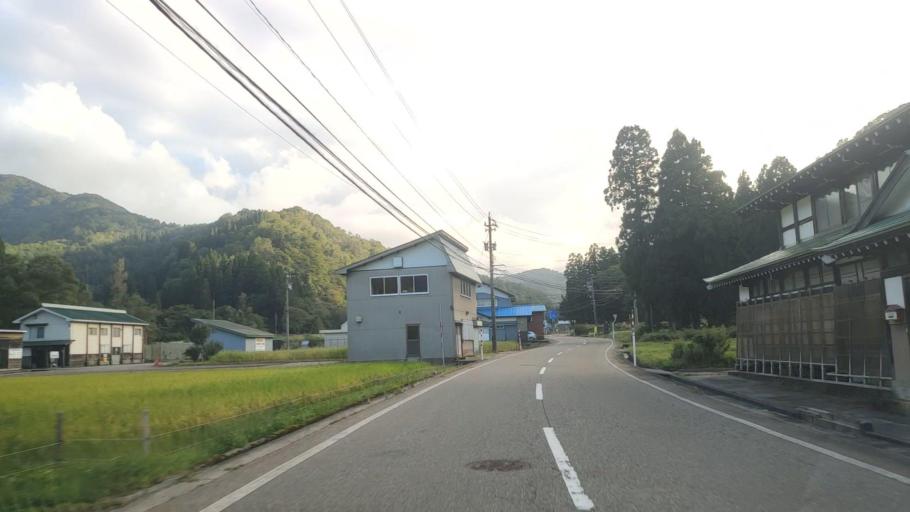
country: JP
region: Toyama
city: Yatsuomachi-higashikumisaka
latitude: 36.4548
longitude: 137.0415
